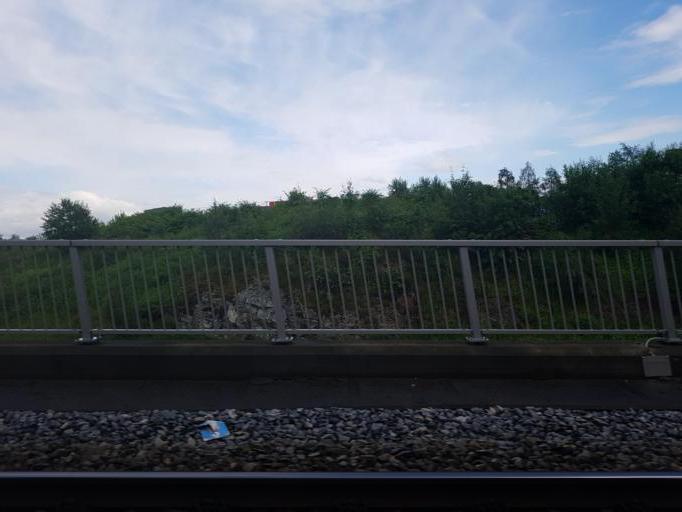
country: NO
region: Hordaland
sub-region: Bergen
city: Ytrebygda
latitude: 60.2918
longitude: 5.2663
